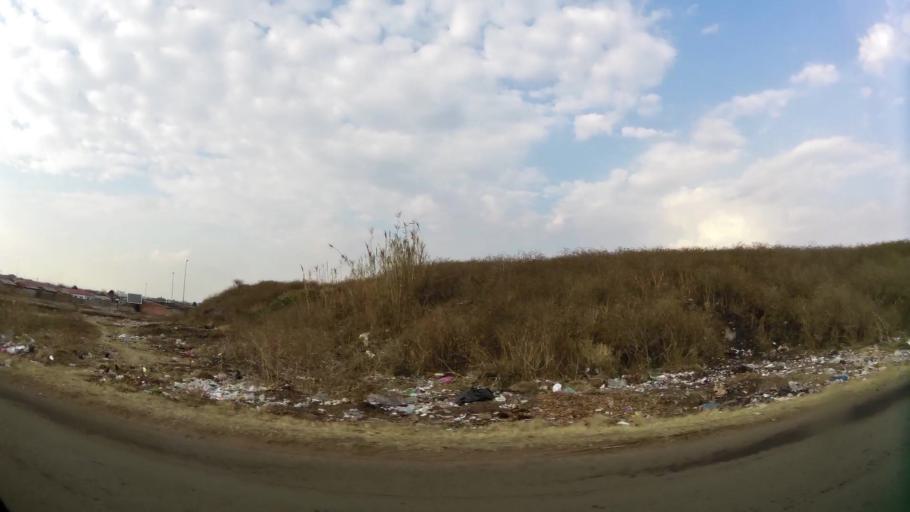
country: ZA
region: Gauteng
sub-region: Sedibeng District Municipality
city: Vereeniging
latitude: -26.6876
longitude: 27.8806
